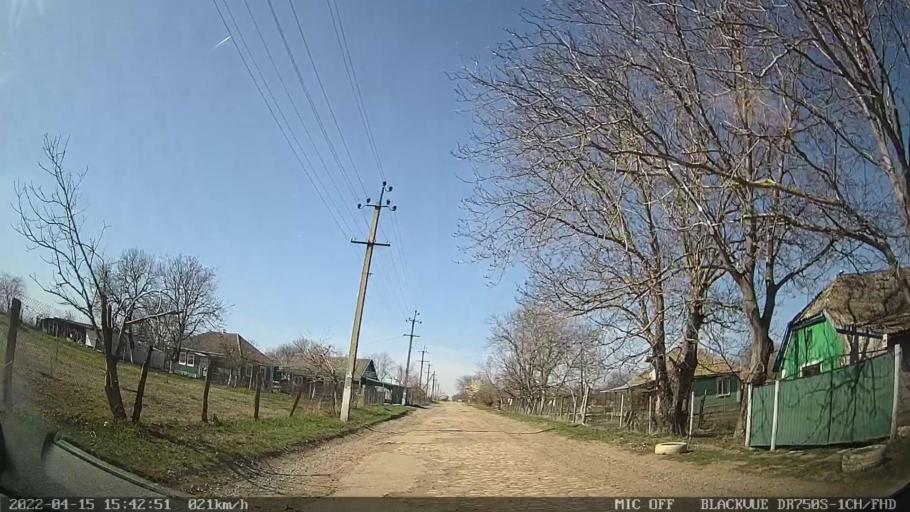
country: MD
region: Raionul Ocnita
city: Otaci
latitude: 48.3634
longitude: 27.9276
